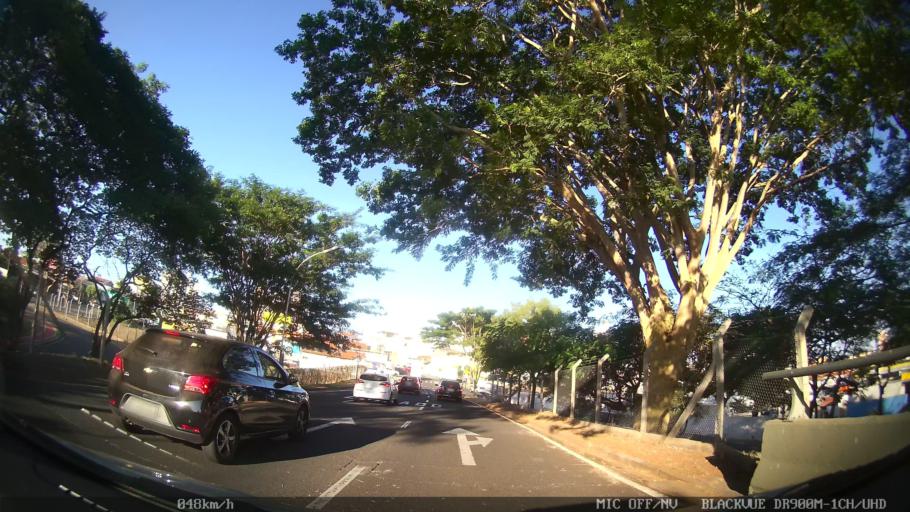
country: BR
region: Sao Paulo
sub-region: Sao Jose Do Rio Preto
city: Sao Jose do Rio Preto
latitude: -20.8043
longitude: -49.3764
